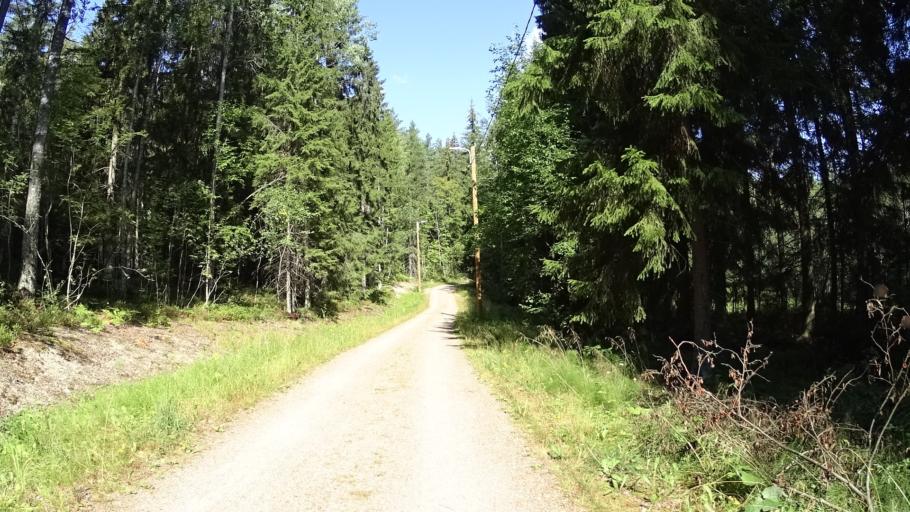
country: FI
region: Uusimaa
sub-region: Helsinki
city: Espoo
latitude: 60.2101
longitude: 24.6222
